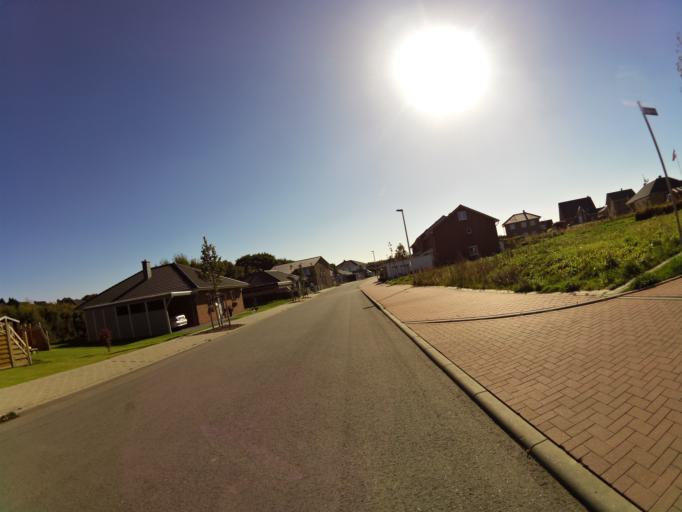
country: DE
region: Schleswig-Holstein
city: Windeby
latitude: 54.4588
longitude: 9.8199
